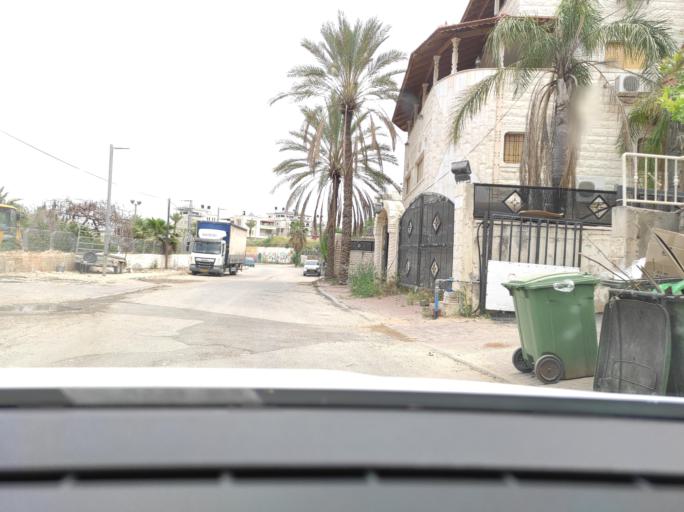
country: IL
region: Central District
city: Kafr Qasim
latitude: 32.1172
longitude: 34.9652
